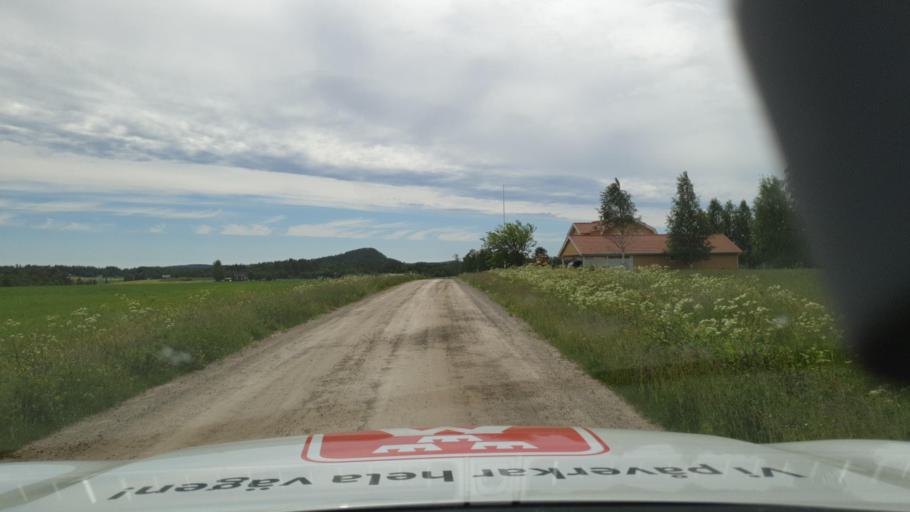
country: SE
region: Vaesterbotten
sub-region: Robertsfors Kommun
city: Robertsfors
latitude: 64.2698
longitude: 20.6313
